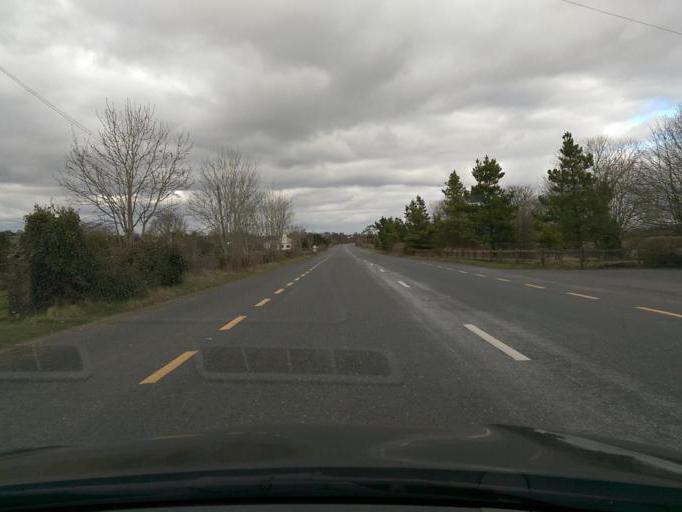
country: IE
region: Connaught
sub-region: County Galway
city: Ballinasloe
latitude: 53.3354
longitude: -8.1358
